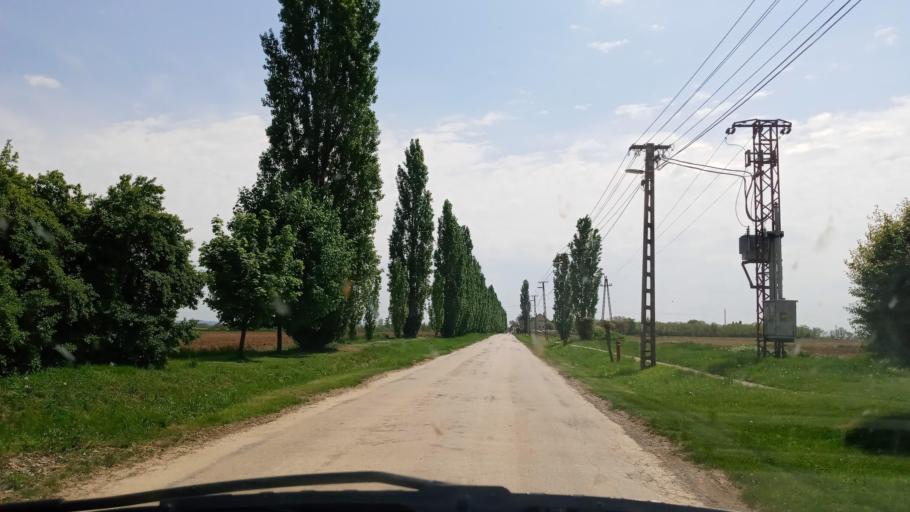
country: HU
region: Baranya
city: Villany
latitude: 45.8815
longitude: 18.5019
